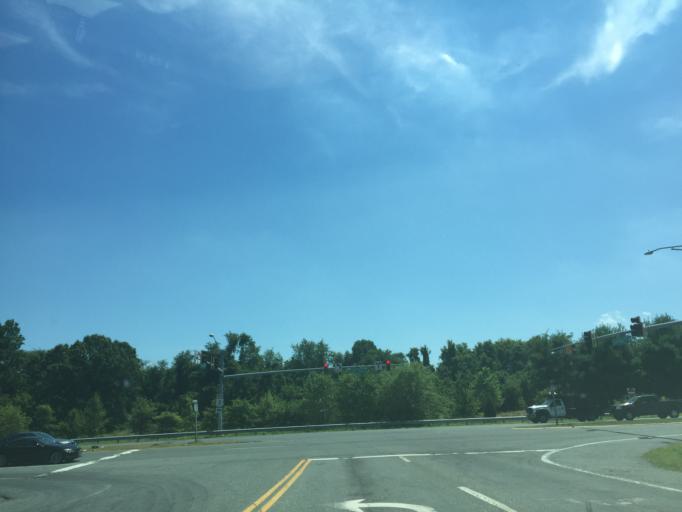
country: US
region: Maryland
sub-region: Harford County
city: Bel Air North
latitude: 39.5701
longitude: -76.3510
